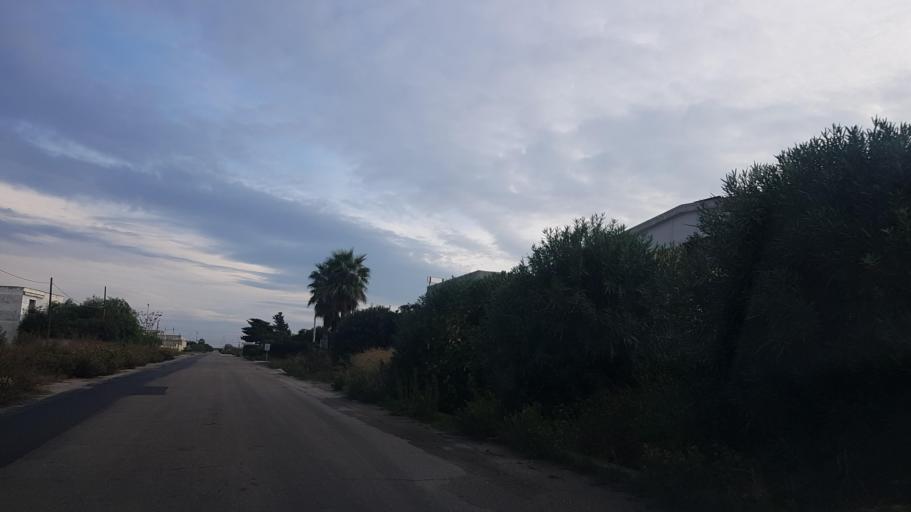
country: IT
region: Apulia
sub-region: Provincia di Brindisi
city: Materdomini
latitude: 40.6302
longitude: 17.9708
